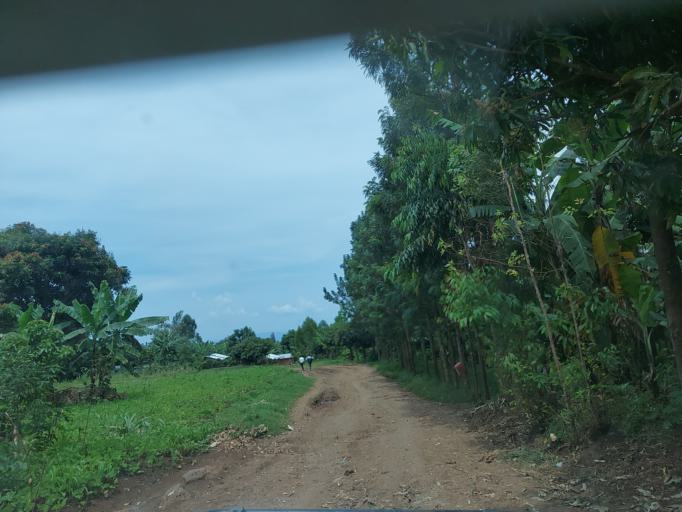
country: CD
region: South Kivu
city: Bukavu
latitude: -2.2380
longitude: 28.8347
